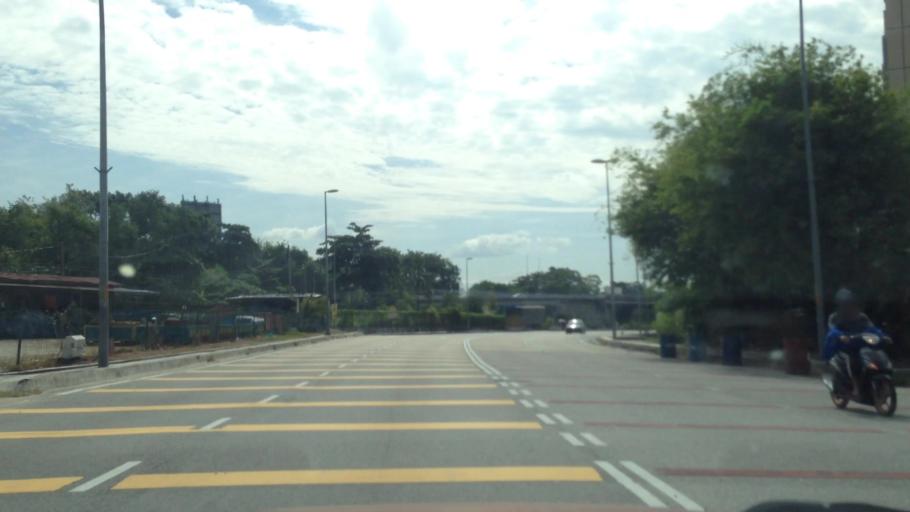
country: MY
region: Selangor
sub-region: Petaling
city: Petaling Jaya
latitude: 3.0840
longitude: 101.6230
